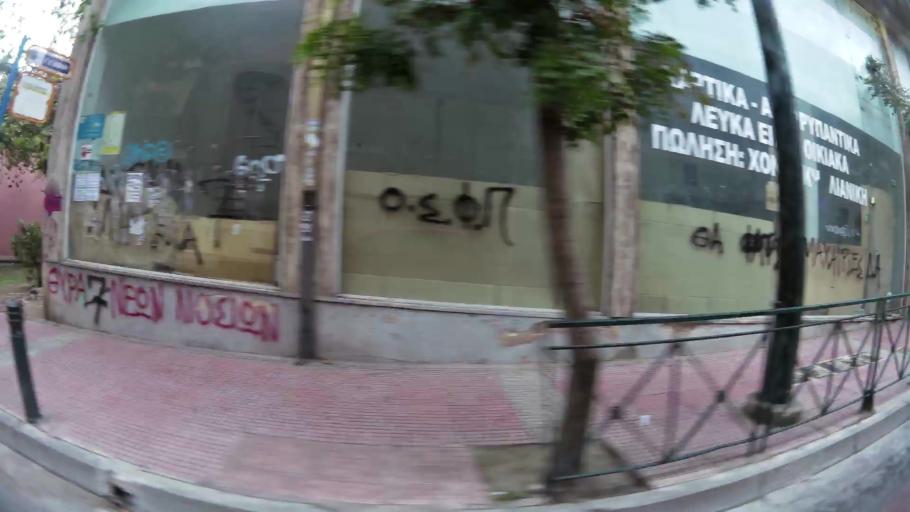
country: GR
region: Attica
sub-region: Nomarchia Athinas
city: Ilion
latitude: 38.0336
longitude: 23.7063
